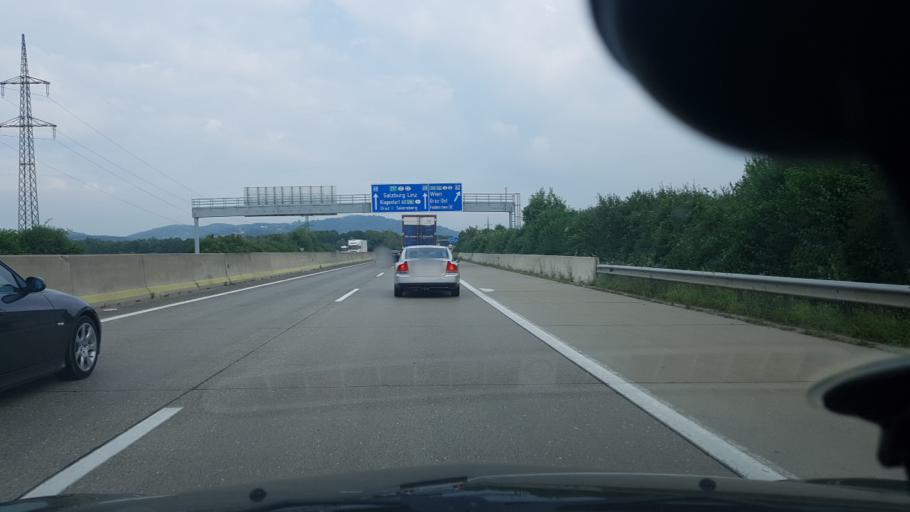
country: AT
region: Styria
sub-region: Politischer Bezirk Graz-Umgebung
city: Seiersberg
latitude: 46.9908
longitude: 15.4135
